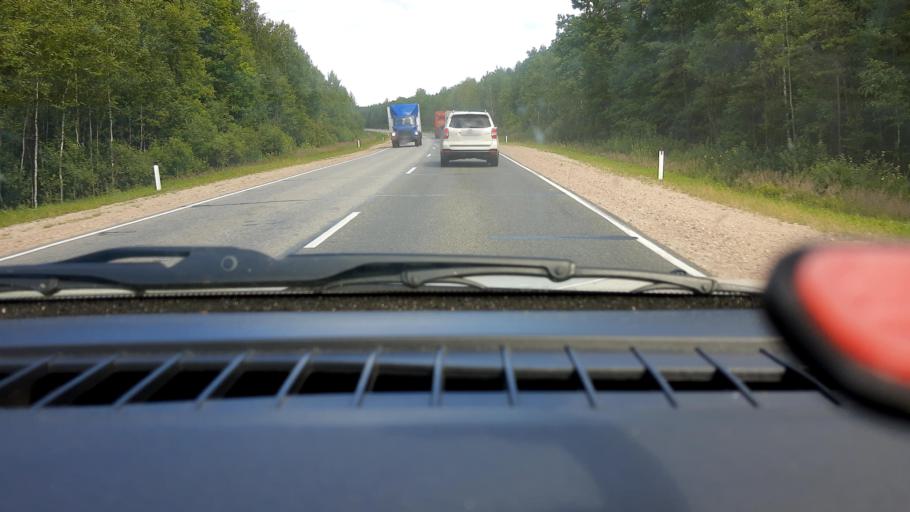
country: RU
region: Nizjnij Novgorod
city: Arzamas
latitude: 55.4126
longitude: 43.9146
